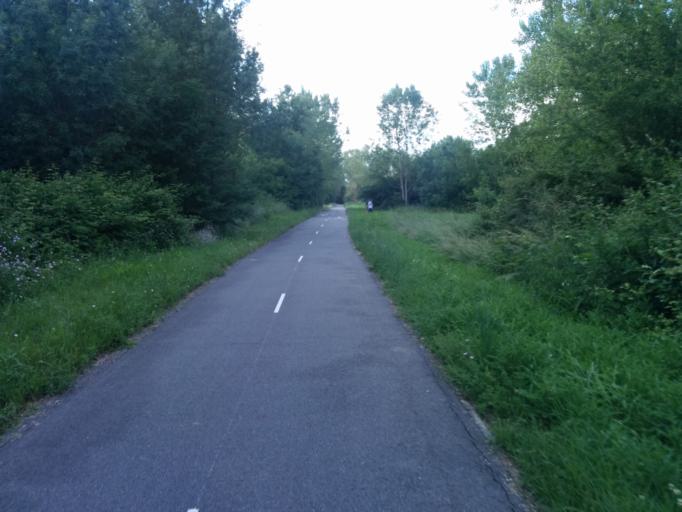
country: FR
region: Midi-Pyrenees
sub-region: Departement de la Haute-Garonne
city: Ramonville-Saint-Agne
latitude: 43.5674
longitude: 1.4950
